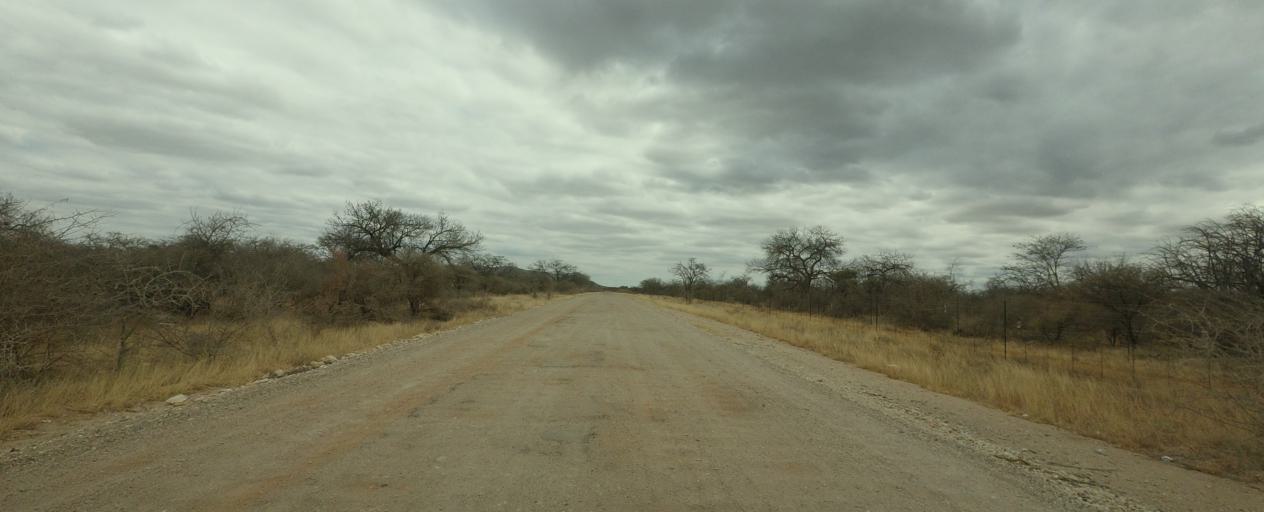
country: BW
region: Central
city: Mogapi
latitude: -22.7814
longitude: 28.3174
